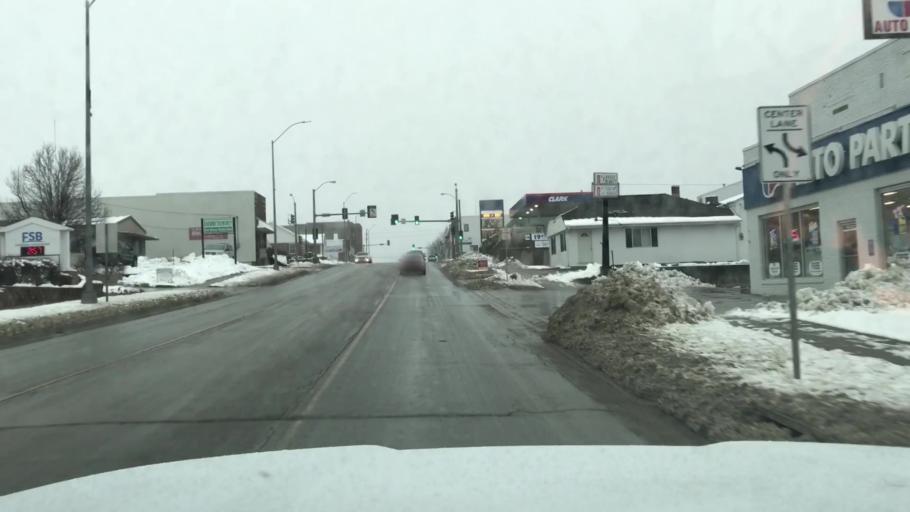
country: US
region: Missouri
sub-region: Clinton County
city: Cameron
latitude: 39.7432
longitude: -94.2358
